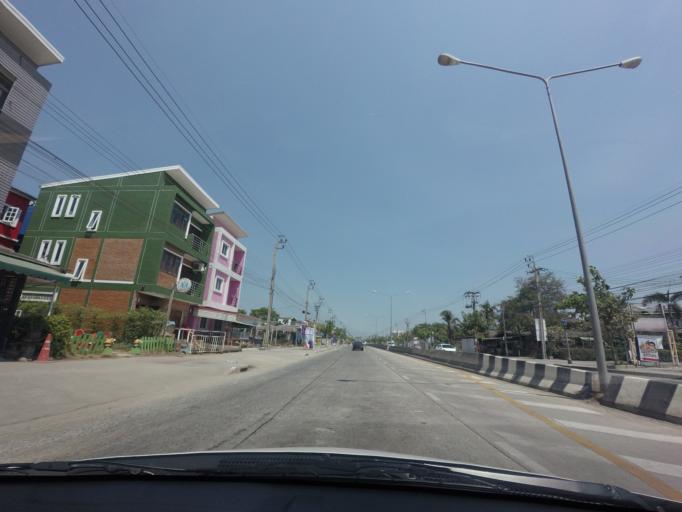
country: TH
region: Bangkok
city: Nong Chok
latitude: 13.8540
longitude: 100.8311
